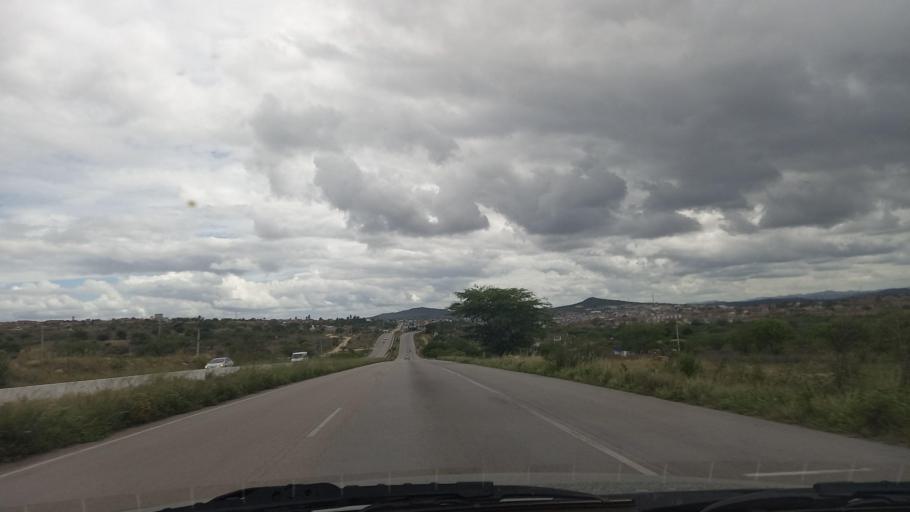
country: BR
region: Pernambuco
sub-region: Caruaru
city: Caruaru
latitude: -8.3264
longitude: -36.1152
